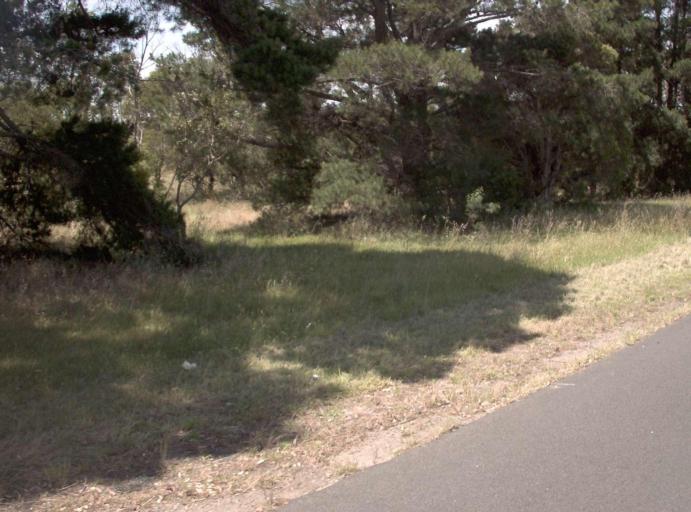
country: AU
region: Victoria
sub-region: Wellington
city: Heyfield
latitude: -38.1581
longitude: 146.7414
